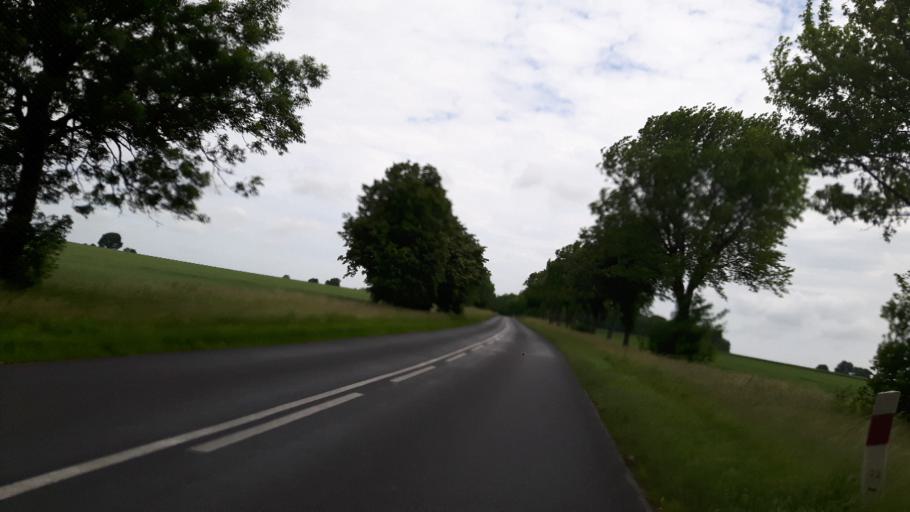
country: PL
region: West Pomeranian Voivodeship
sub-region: Powiat gryficki
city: Gryfice
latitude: 53.9500
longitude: 15.2255
